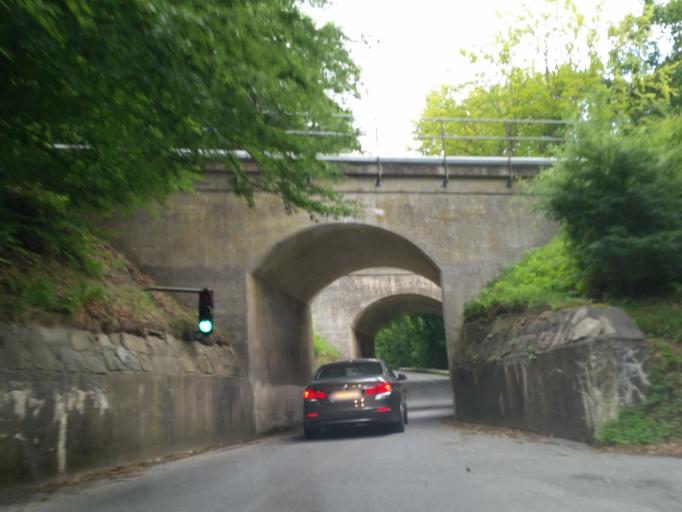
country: DK
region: South Denmark
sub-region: Vejle Kommune
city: Borkop
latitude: 55.6922
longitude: 9.6163
